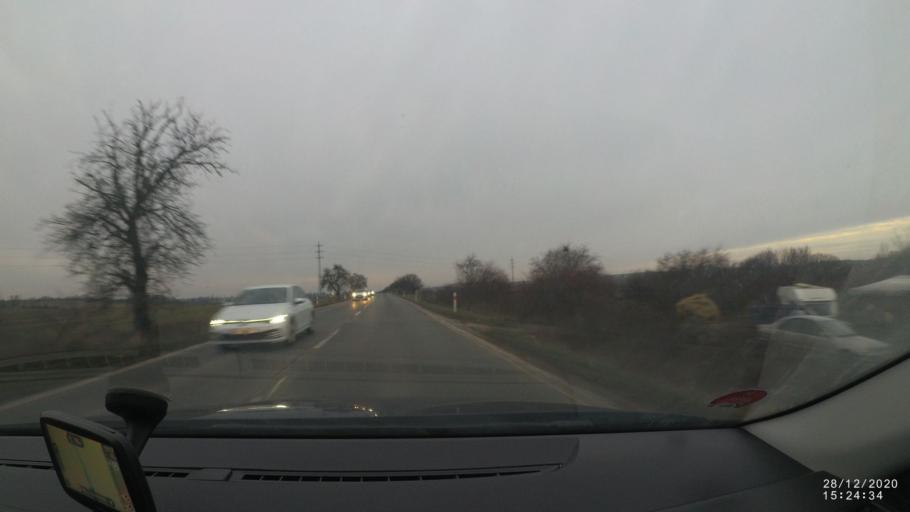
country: CZ
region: Praha
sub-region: Praha 20
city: Horni Pocernice
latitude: 50.0797
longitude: 14.6381
